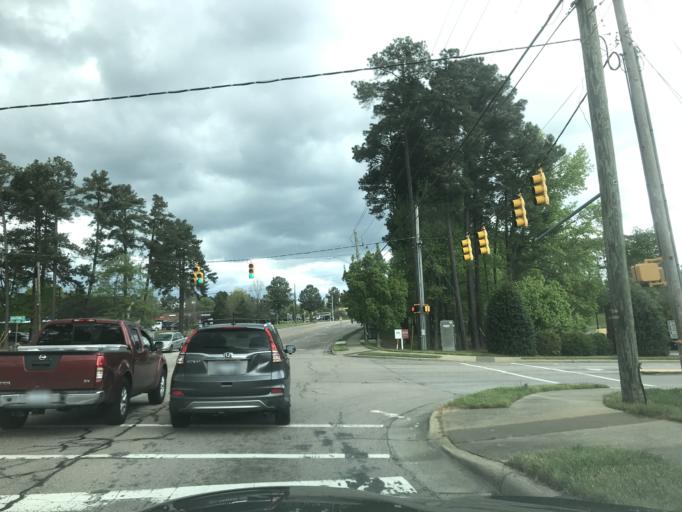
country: US
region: North Carolina
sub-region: Wake County
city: West Raleigh
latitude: 35.7835
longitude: -78.7218
